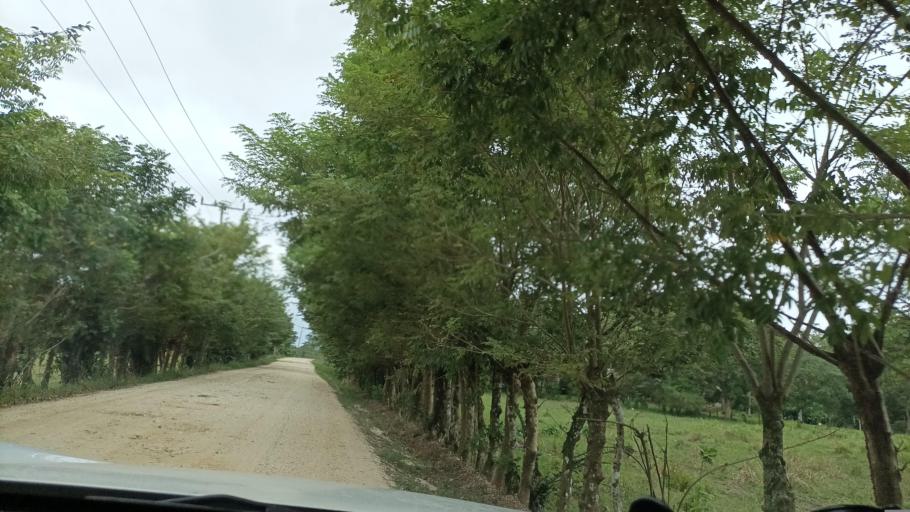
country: MX
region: Veracruz
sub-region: Moloacan
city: Cuichapa
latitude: 17.8372
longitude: -94.3550
